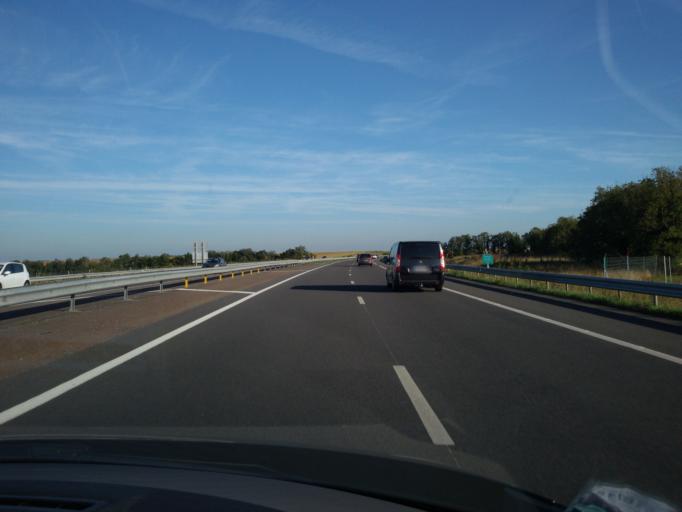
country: FR
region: Centre
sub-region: Departement du Cher
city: Plaimpied-Givaudins
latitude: 46.9873
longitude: 2.4117
